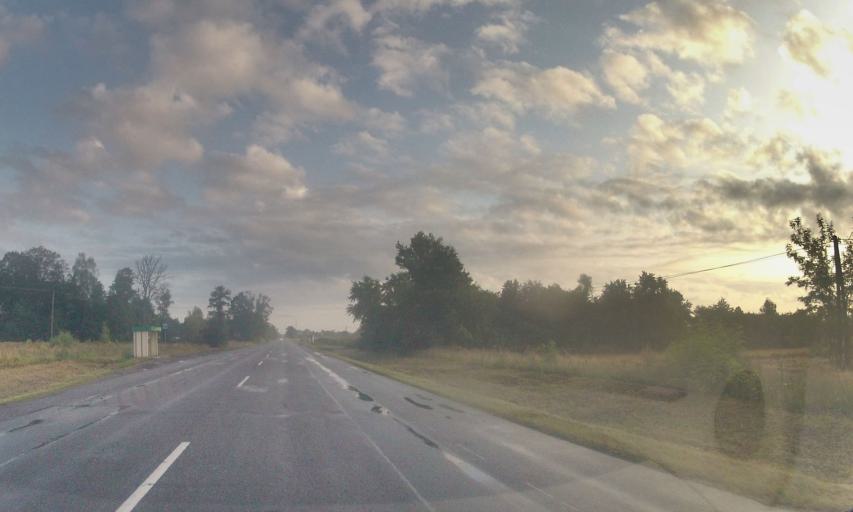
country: PL
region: Masovian Voivodeship
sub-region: Powiat plonski
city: Baboszewo
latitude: 52.7352
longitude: 20.3203
